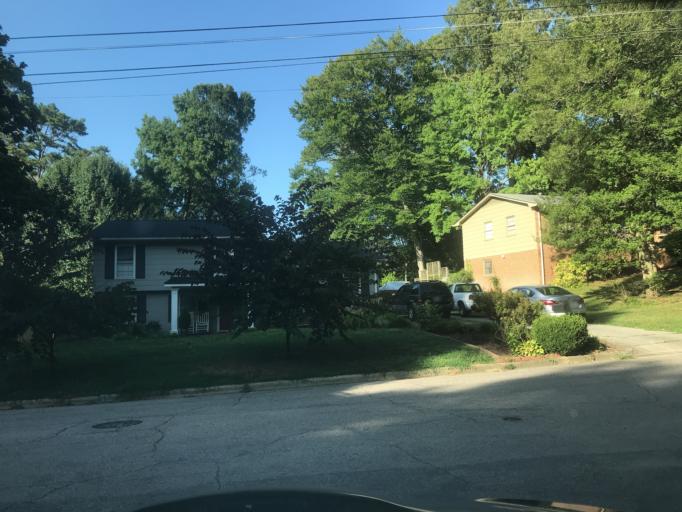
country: US
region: North Carolina
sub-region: Wake County
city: West Raleigh
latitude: 35.8448
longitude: -78.6343
